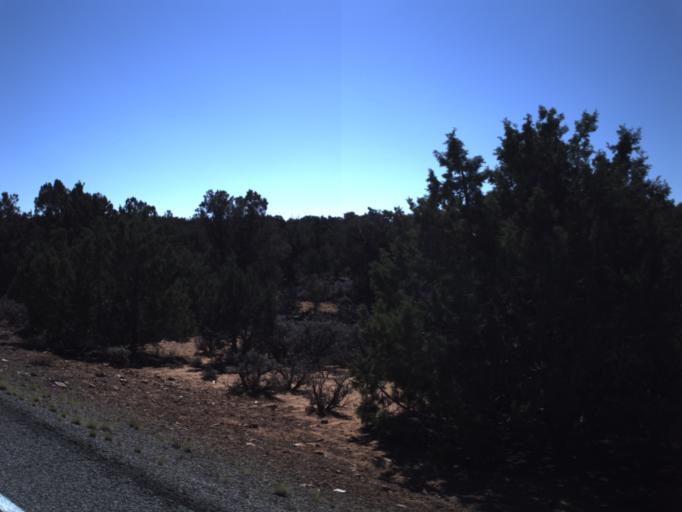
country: US
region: Utah
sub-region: San Juan County
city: Blanding
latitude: 37.5521
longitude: -109.9937
